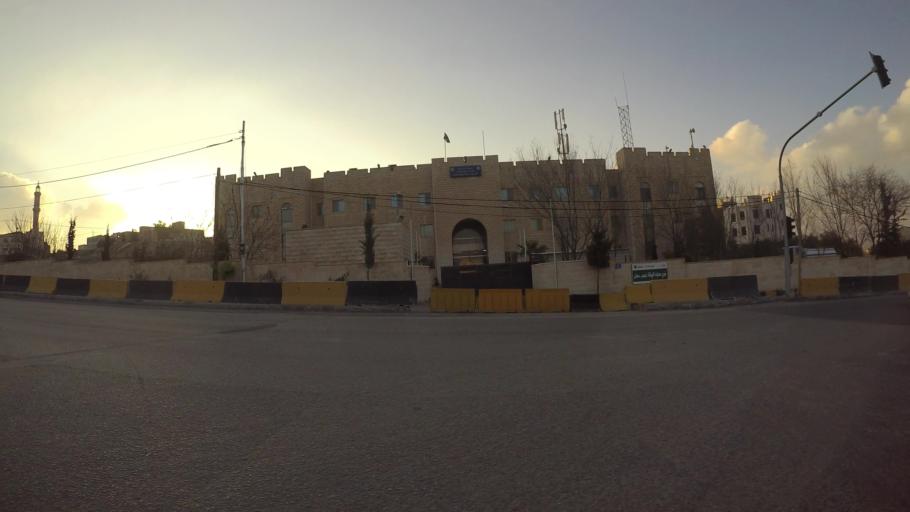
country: JO
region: Amman
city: Al Bunayyat ash Shamaliyah
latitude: 31.9050
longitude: 35.9205
